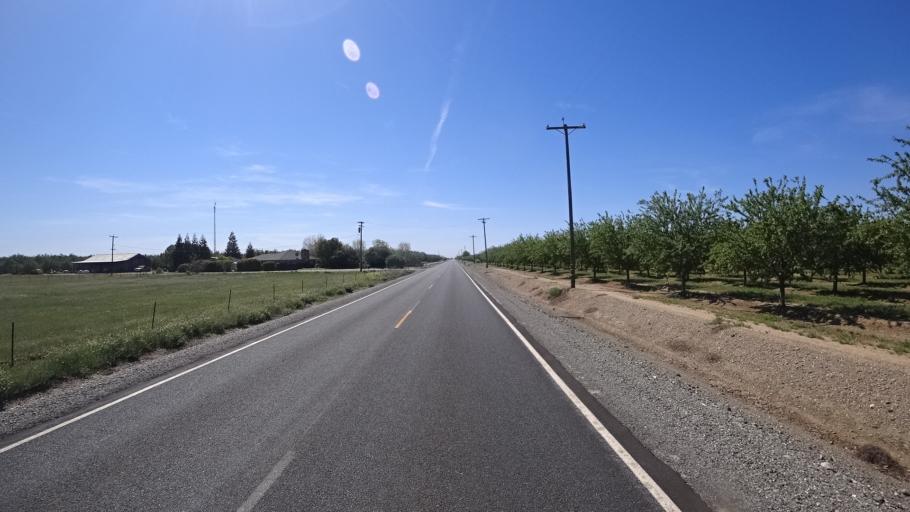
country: US
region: California
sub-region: Glenn County
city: Orland
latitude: 39.6790
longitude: -122.1406
